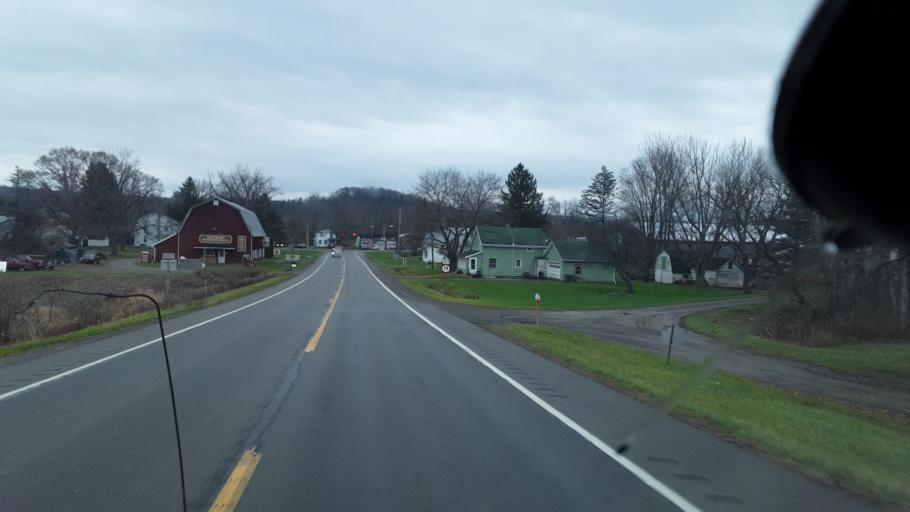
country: US
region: New York
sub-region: Allegany County
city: Houghton
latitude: 42.3889
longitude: -78.1561
